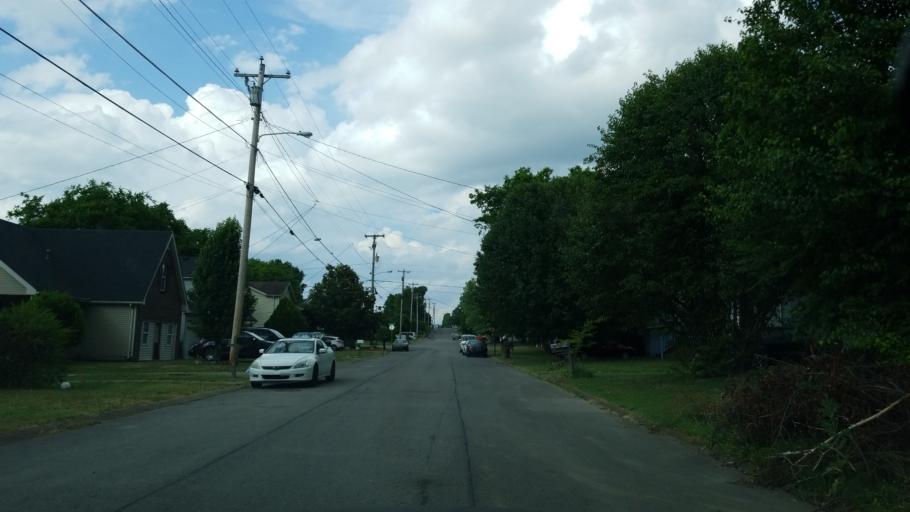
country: US
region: Tennessee
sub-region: Rutherford County
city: La Vergne
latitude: 36.0796
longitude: -86.6106
